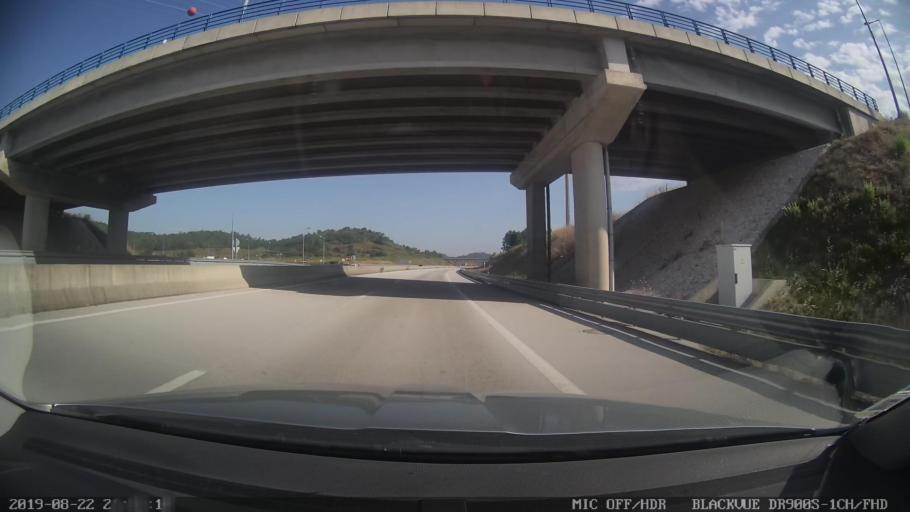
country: PT
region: Coimbra
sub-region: Penela
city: Penela
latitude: 40.0781
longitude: -8.3851
